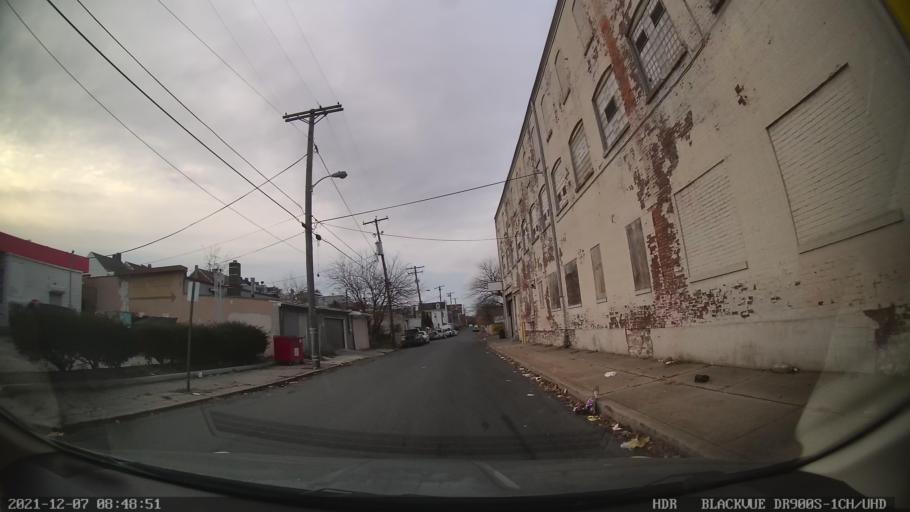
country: US
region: Pennsylvania
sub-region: Berks County
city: Reading
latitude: 40.3502
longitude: -75.9208
